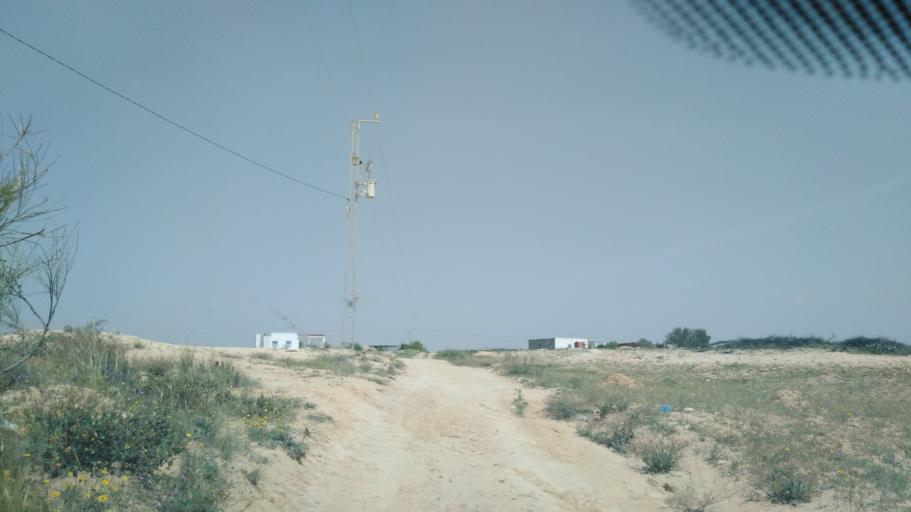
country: TN
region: Safaqis
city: Sfax
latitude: 34.7453
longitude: 10.5694
